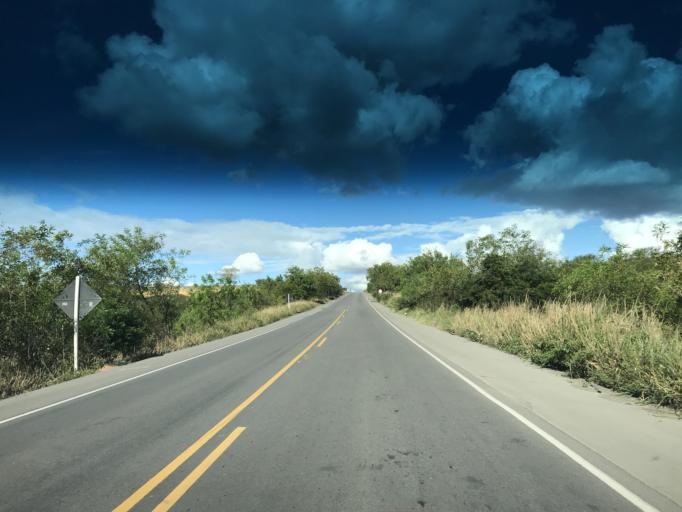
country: BR
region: Bahia
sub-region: Ruy Barbosa
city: Terra Nova
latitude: -12.4455
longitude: -40.7209
